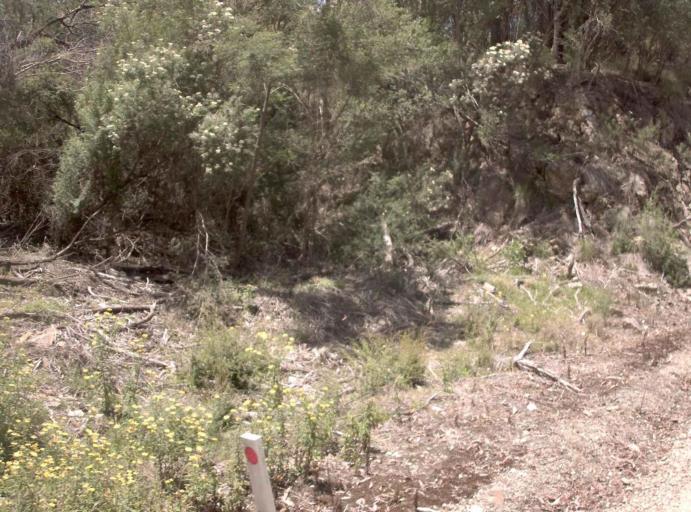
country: AU
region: Victoria
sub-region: East Gippsland
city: Lakes Entrance
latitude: -37.5600
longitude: 147.8861
